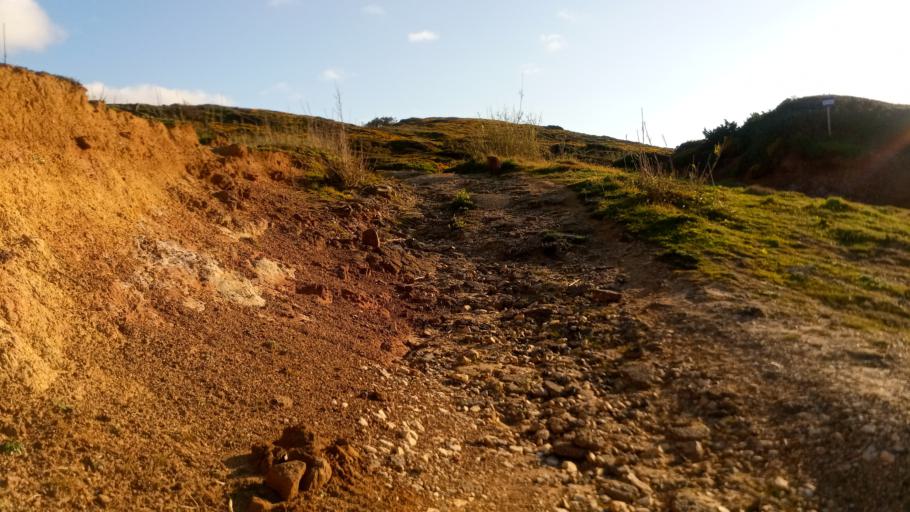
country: PT
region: Leiria
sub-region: Caldas da Rainha
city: Caldas da Rainha
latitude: 39.5031
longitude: -9.1598
